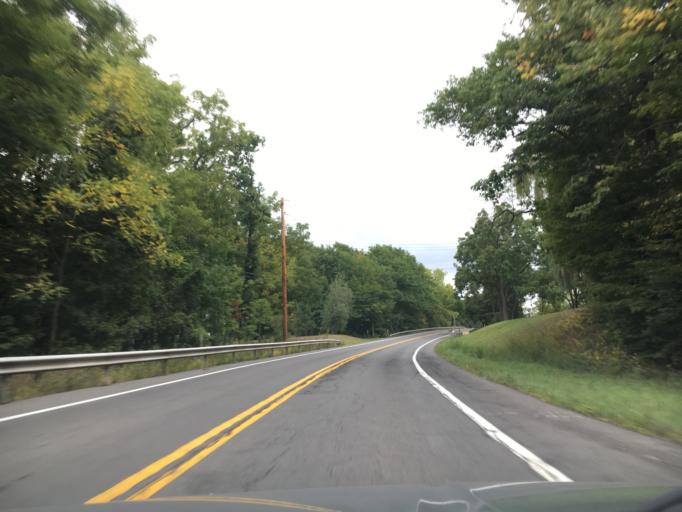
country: US
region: New York
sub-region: Tompkins County
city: Trumansburg
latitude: 42.6687
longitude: -76.7300
